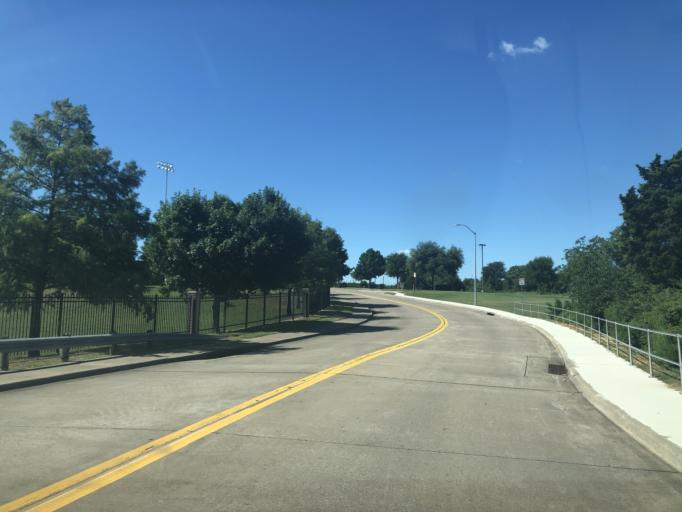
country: US
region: Texas
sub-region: Dallas County
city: Duncanville
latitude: 32.6618
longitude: -96.9330
